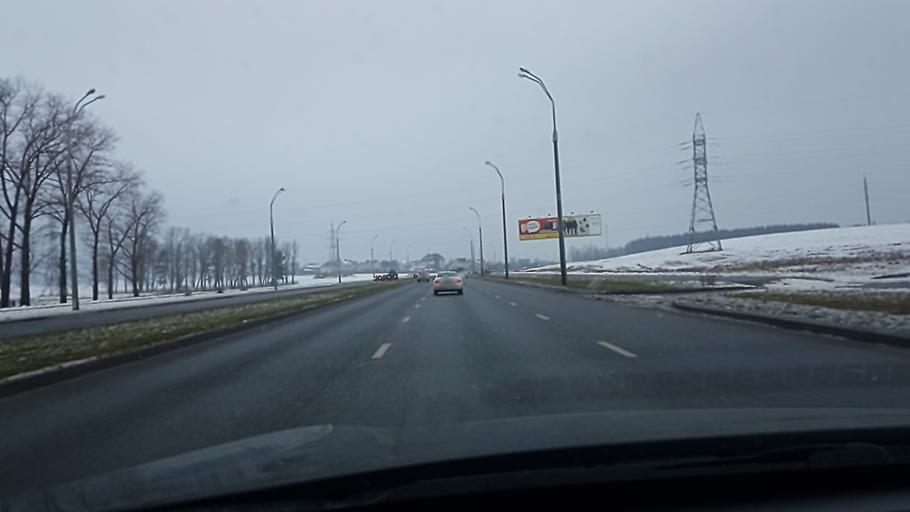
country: BY
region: Minsk
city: Minsk
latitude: 53.9467
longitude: 27.5379
